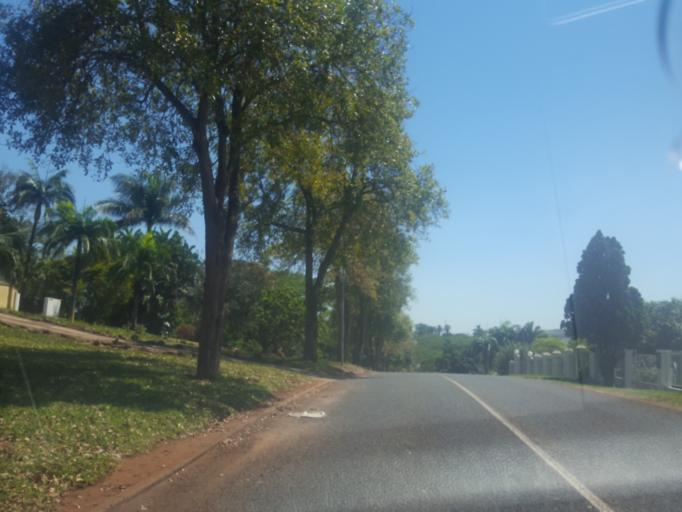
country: ZA
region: KwaZulu-Natal
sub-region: uThungulu District Municipality
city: Empangeni
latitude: -28.7461
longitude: 31.9021
